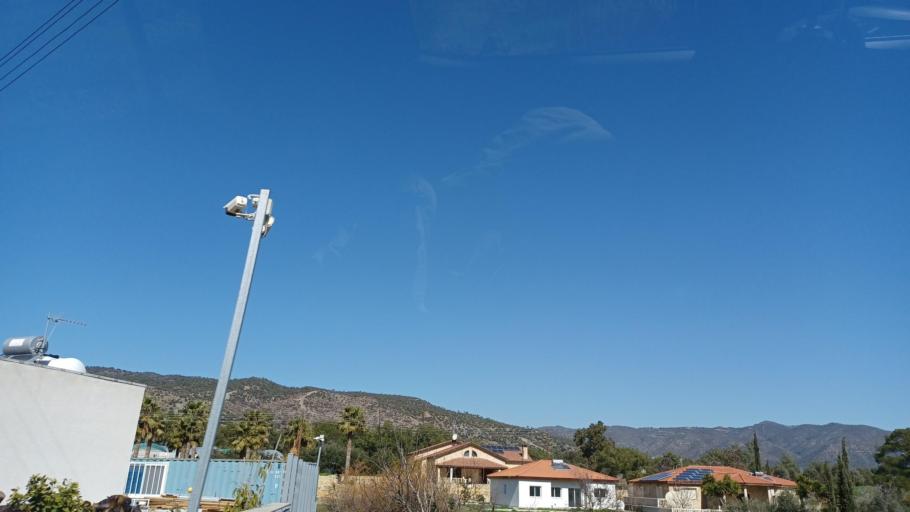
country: CY
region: Limassol
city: Parekklisha
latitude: 34.7524
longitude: 33.1430
